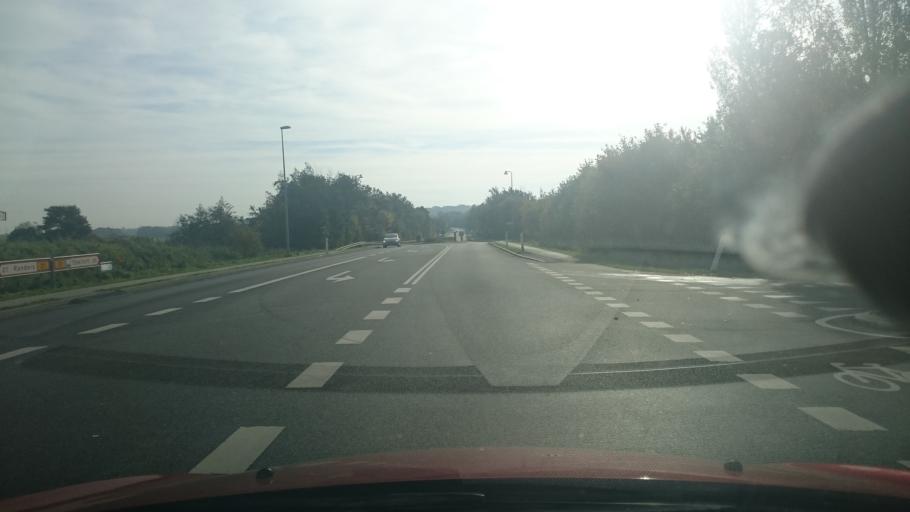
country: DK
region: Central Jutland
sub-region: Syddjurs Kommune
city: Hornslet
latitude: 56.3330
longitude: 10.3849
